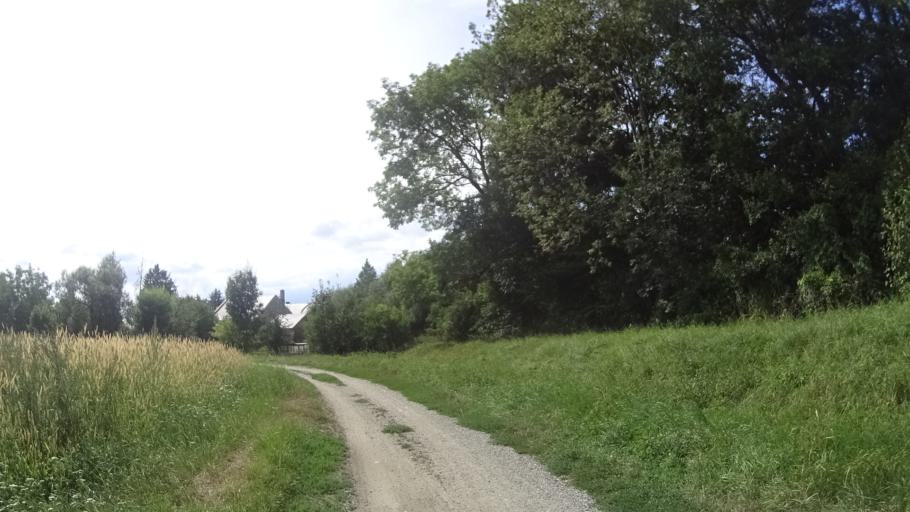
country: CZ
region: Olomoucky
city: Naklo
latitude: 49.6787
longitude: 17.1469
